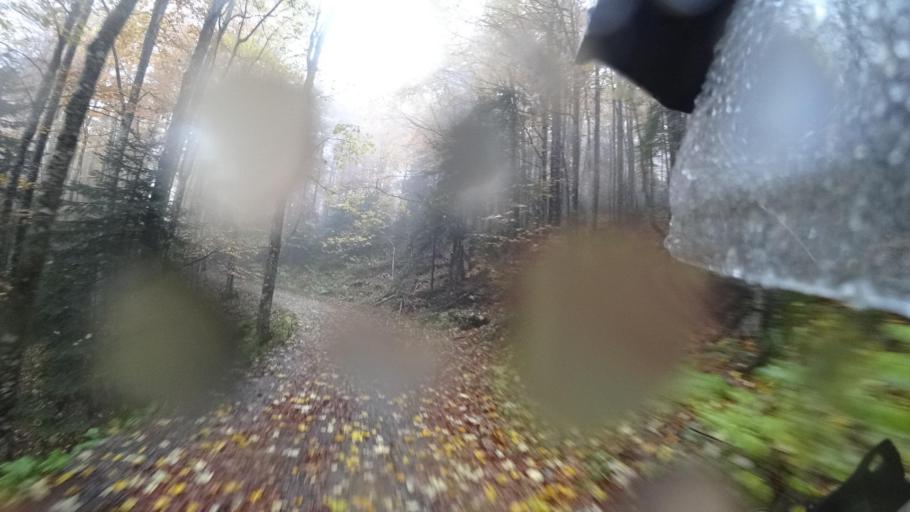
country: HR
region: Primorsko-Goranska
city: Vrbovsko
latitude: 45.3018
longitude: 15.0542
